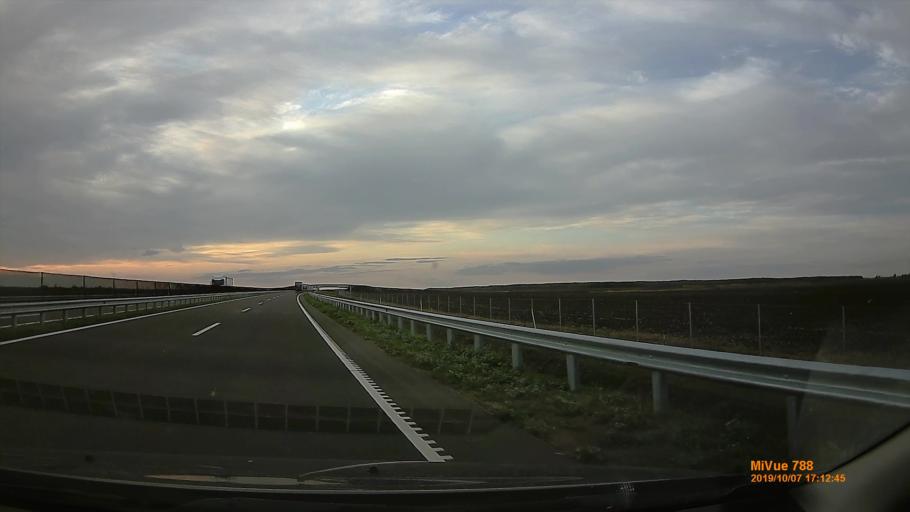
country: HU
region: Jasz-Nagykun-Szolnok
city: Ocsod
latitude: 46.8157
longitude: 20.3821
